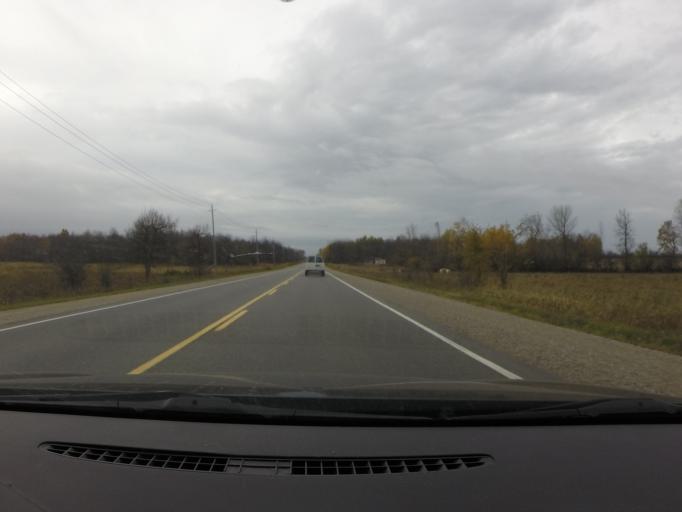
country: CA
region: Ontario
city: Perth
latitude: 44.9509
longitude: -76.2357
